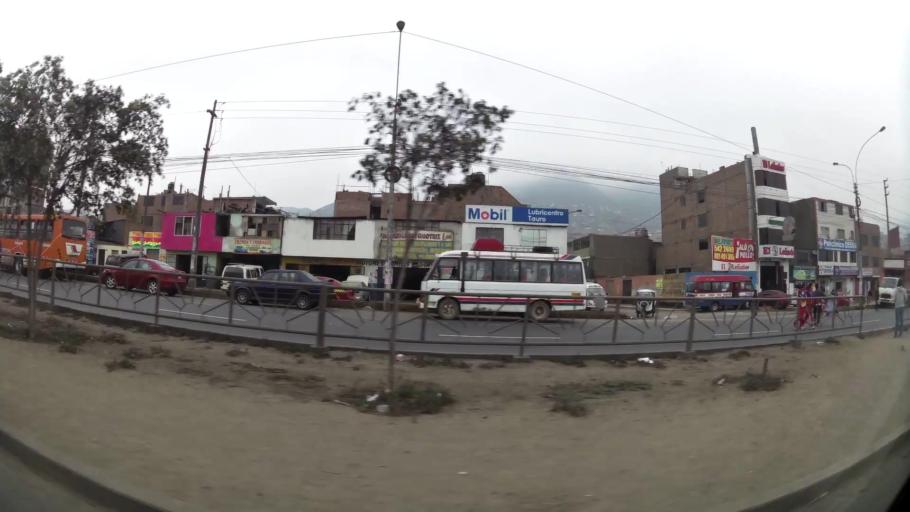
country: PE
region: Lima
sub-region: Lima
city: Urb. Santo Domingo
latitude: -11.9268
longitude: -77.0429
